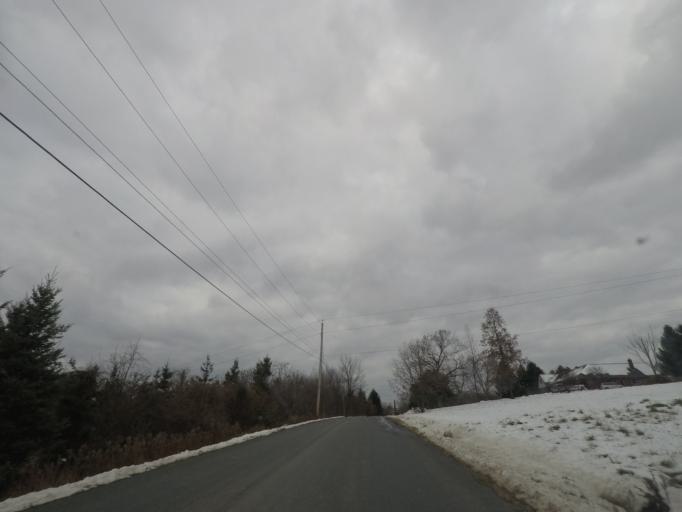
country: US
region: New York
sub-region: Rensselaer County
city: West Sand Lake
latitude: 42.5962
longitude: -73.6311
